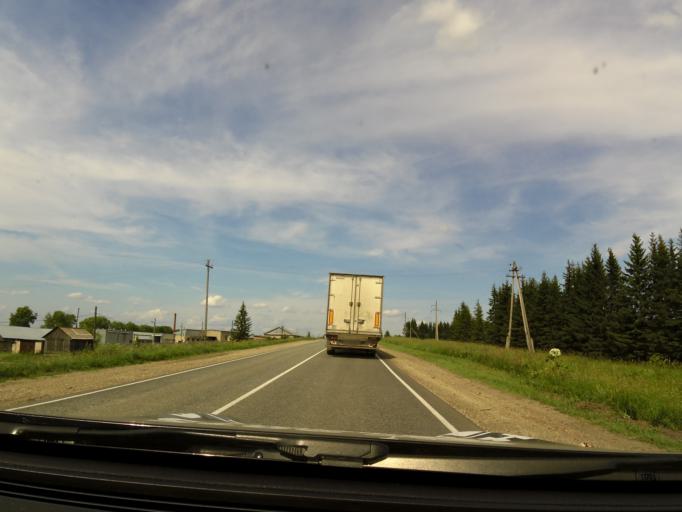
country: RU
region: Kirov
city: Slobodskoy
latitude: 58.7500
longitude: 50.3131
